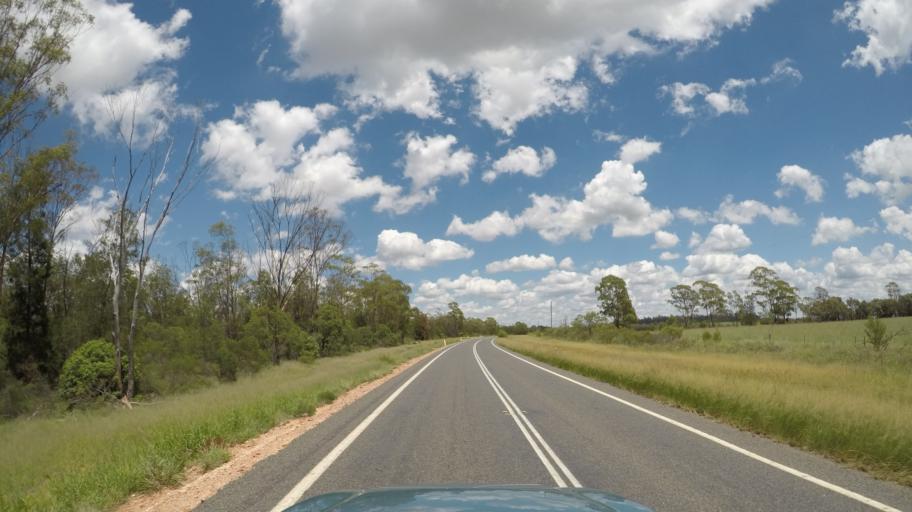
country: AU
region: Queensland
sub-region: Goondiwindi
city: Goondiwindi
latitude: -28.0076
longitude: 150.9213
